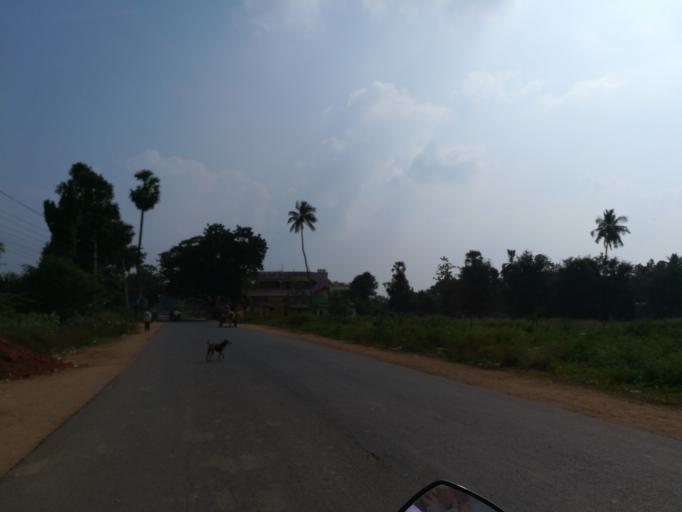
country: IN
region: Andhra Pradesh
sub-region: Nellore
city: Kovur
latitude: 14.5522
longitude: 79.9904
